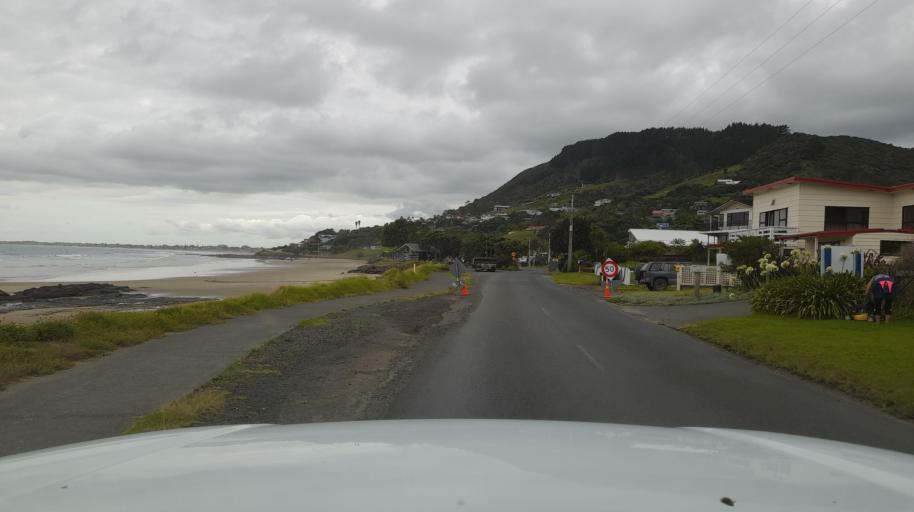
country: NZ
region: Northland
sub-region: Far North District
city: Ahipara
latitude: -35.1783
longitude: 173.1327
